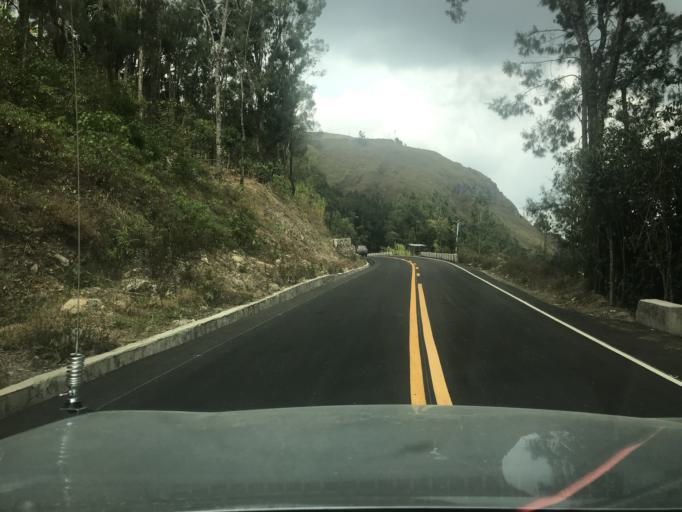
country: TL
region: Manufahi
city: Same
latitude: -8.8931
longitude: 125.5922
